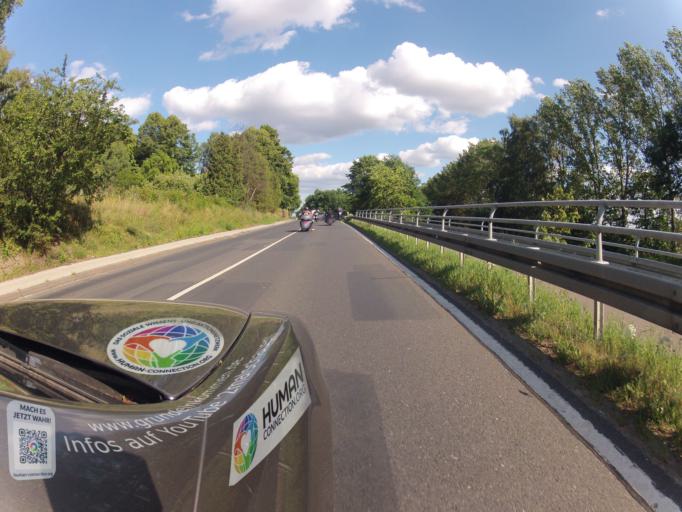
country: DE
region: Mecklenburg-Vorpommern
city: Seebad Bansin
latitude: 53.9661
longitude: 14.1258
